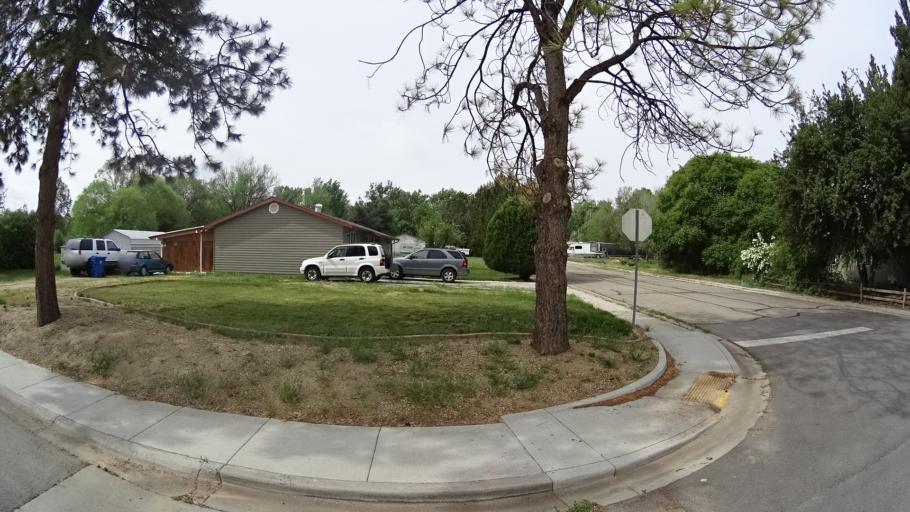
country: US
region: Idaho
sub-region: Ada County
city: Meridian
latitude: 43.5357
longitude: -116.3103
